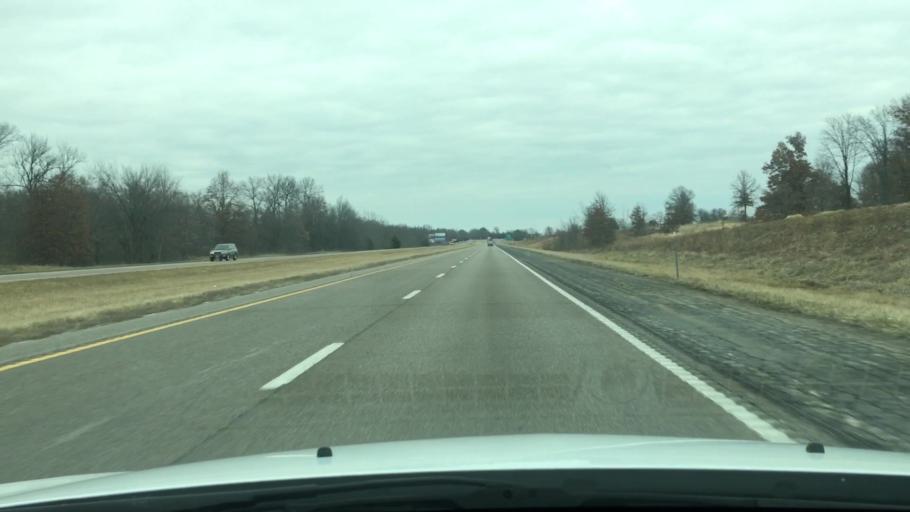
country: US
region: Missouri
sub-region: Callaway County
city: Fulton
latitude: 38.9963
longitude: -91.8934
